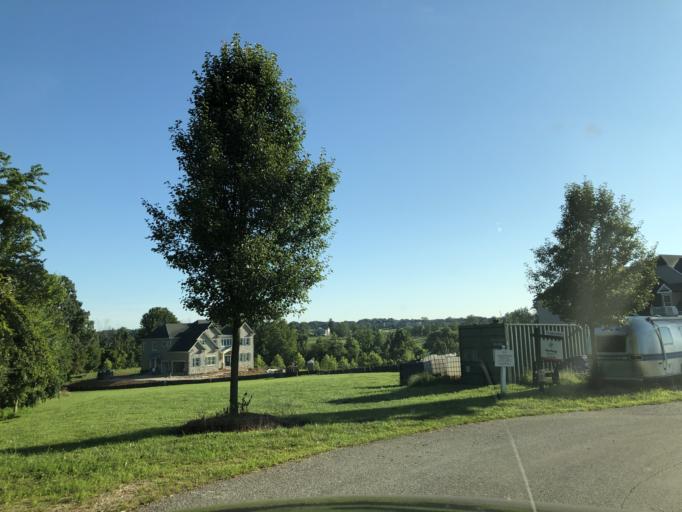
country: US
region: Maryland
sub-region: Howard County
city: Highland
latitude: 39.1954
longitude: -76.9545
